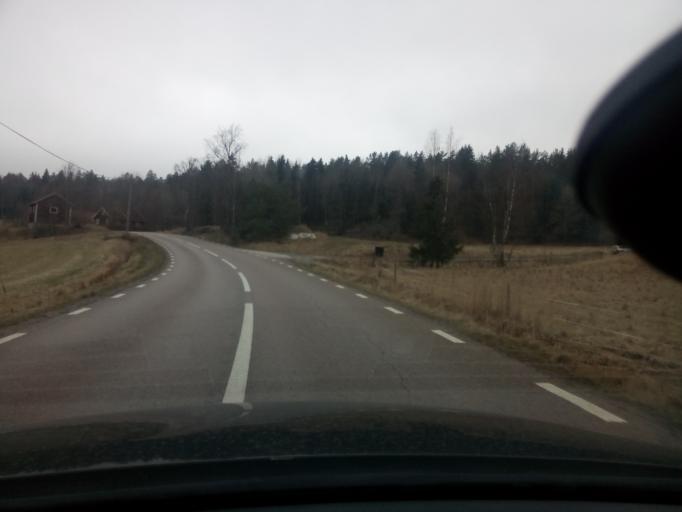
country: SE
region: Soedermanland
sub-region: Strangnas Kommun
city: Akers Styckebruk
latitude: 59.1227
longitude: 17.1336
